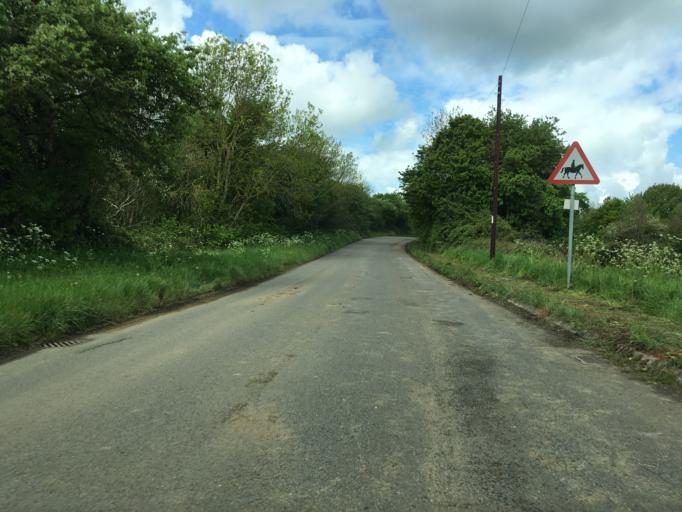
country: GB
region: England
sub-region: Gloucestershire
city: Stonehouse
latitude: 51.7781
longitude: -2.3059
